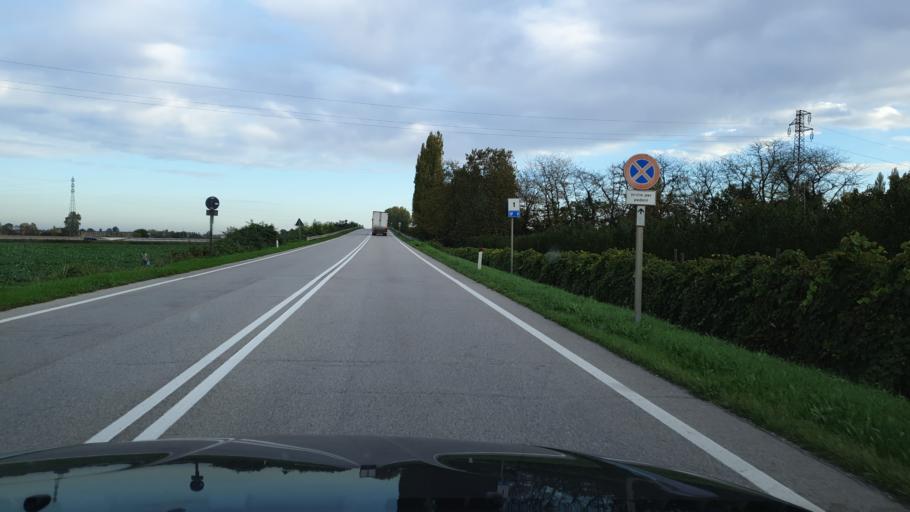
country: IT
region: Veneto
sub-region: Provincia di Padova
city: Monselice
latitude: 45.2362
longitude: 11.7711
